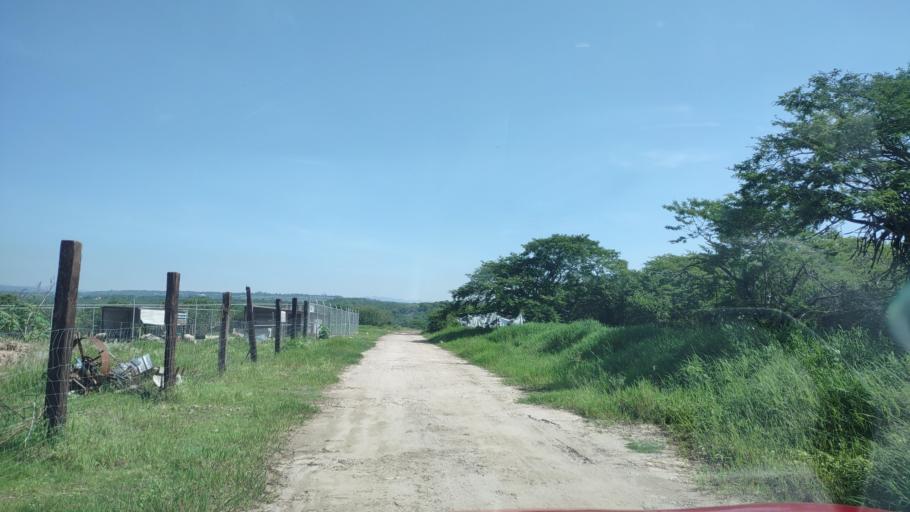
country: MX
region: Veracruz
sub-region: Emiliano Zapata
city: Dos Rios
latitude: 19.4331
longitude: -96.8037
